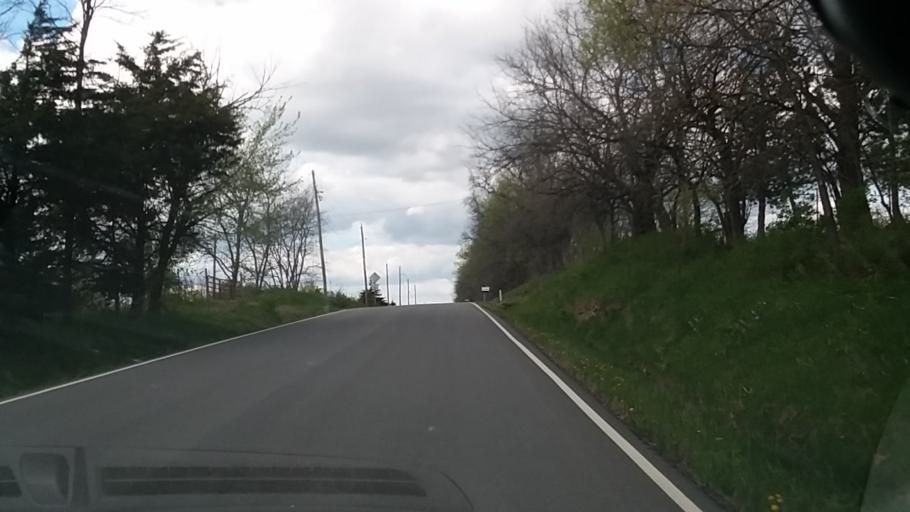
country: US
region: Kansas
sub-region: Douglas County
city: Lawrence
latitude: 38.8923
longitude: -95.2418
